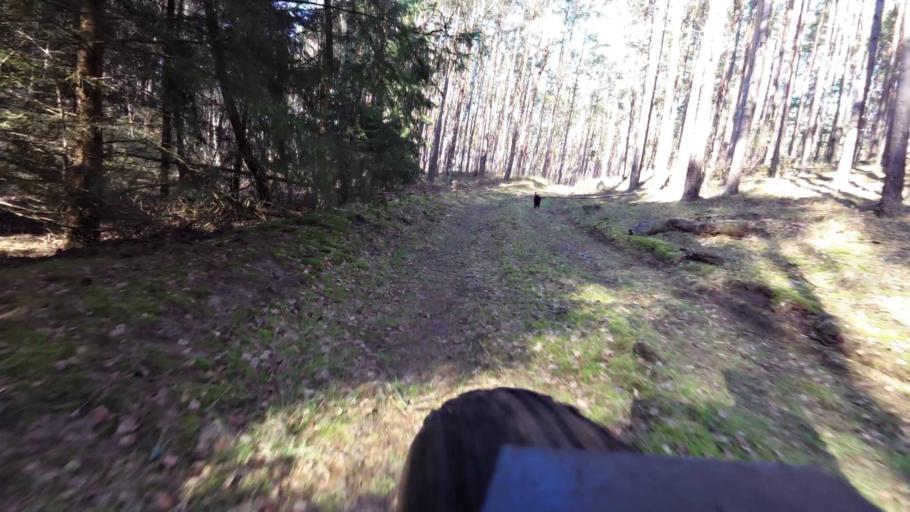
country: PL
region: Lubusz
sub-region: Powiat sulecinski
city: Torzym
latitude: 52.2177
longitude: 15.0103
